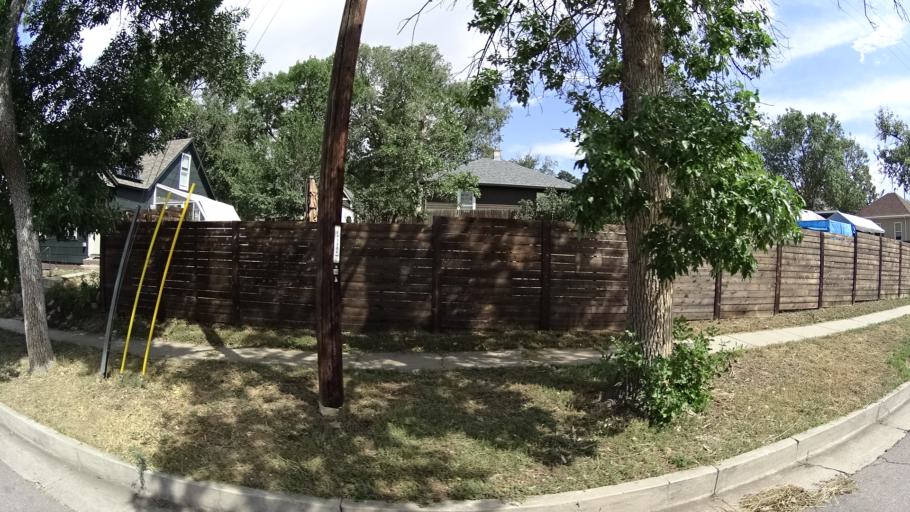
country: US
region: Colorado
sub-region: El Paso County
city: Colorado Springs
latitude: 38.8359
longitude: -104.8105
